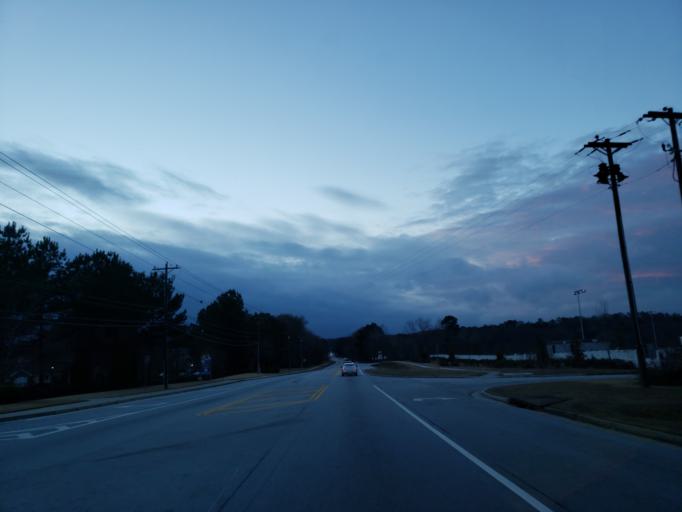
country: US
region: Georgia
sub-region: Douglas County
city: Lithia Springs
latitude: 33.6930
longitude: -84.6248
